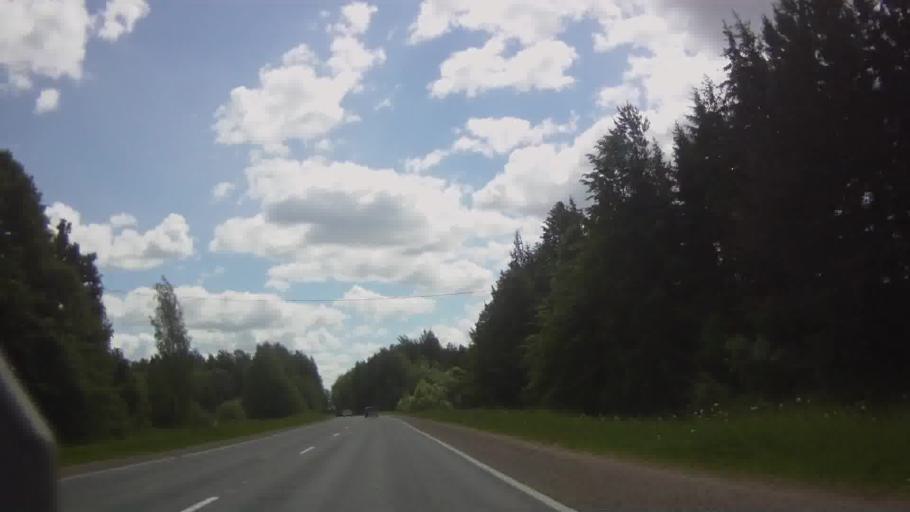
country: LV
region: Vilanu
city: Vilani
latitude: 56.5876
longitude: 26.8855
